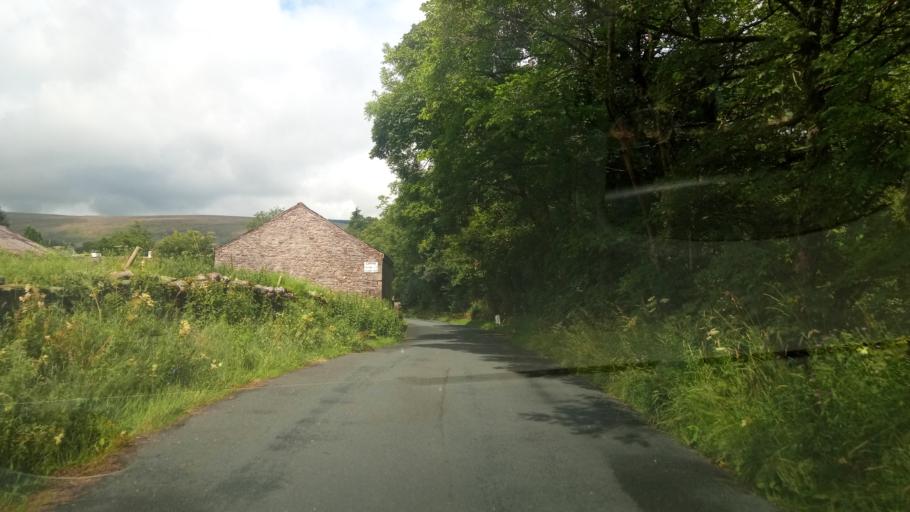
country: GB
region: England
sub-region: North Yorkshire
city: Ingleton
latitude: 54.2712
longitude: -2.3559
